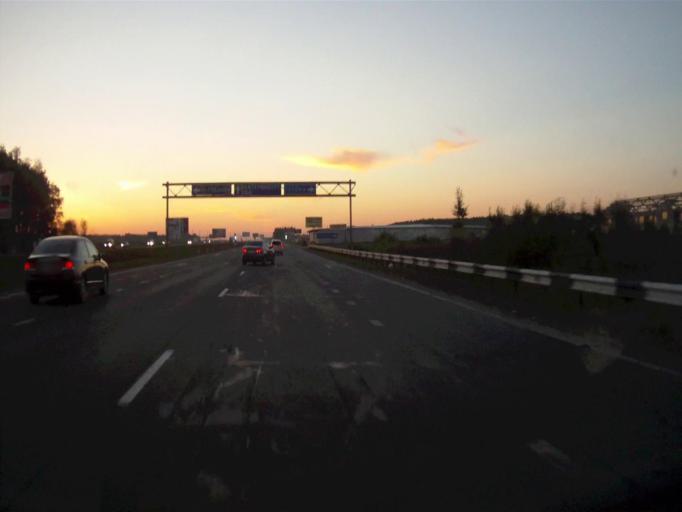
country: RU
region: Chelyabinsk
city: Roshchino
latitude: 55.1842
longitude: 61.2446
